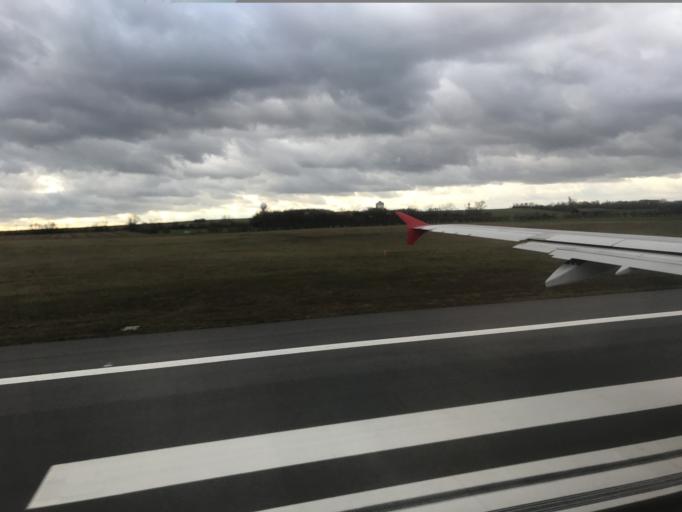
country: AT
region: Lower Austria
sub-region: Politischer Bezirk Bruck an der Leitha
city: Enzersdorf an der Fischa
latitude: 48.1113
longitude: 16.5696
